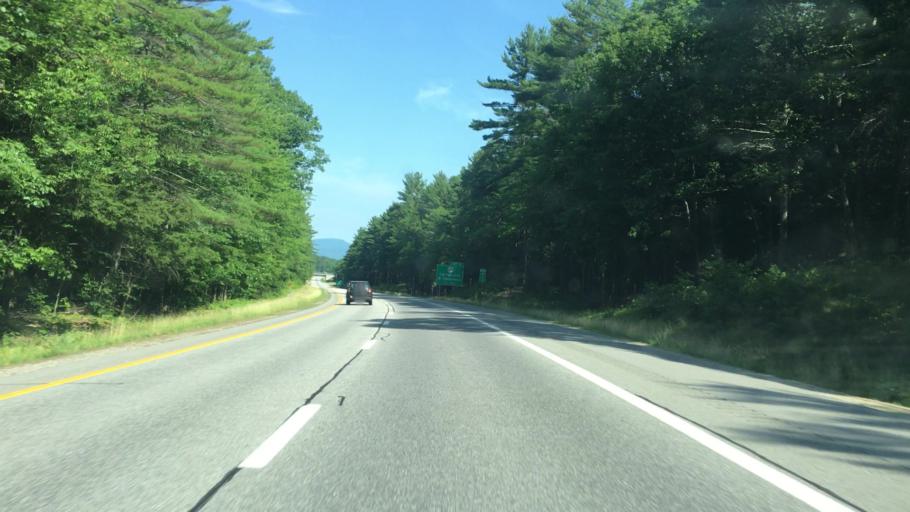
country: US
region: New Hampshire
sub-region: Merrimack County
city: Hopkinton
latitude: 43.1946
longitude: -71.7006
